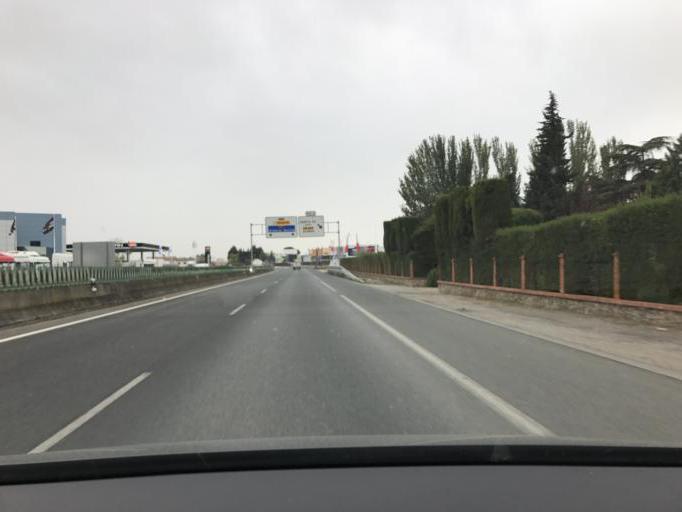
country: ES
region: Andalusia
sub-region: Provincia de Granada
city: Atarfe
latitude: 37.1930
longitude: -3.6971
